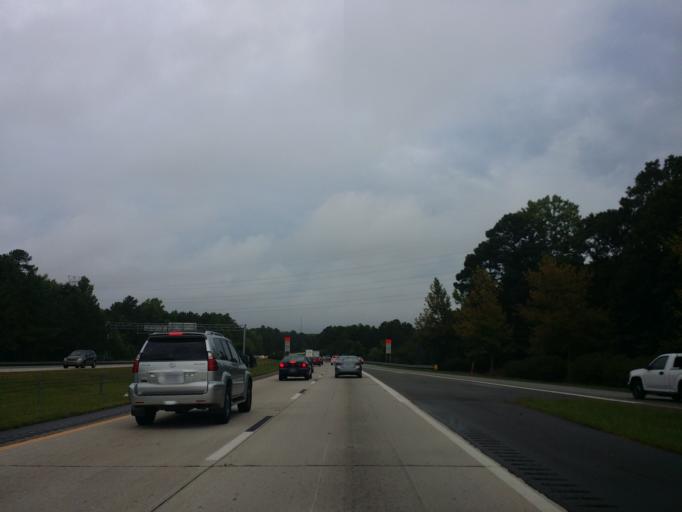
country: US
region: North Carolina
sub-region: Durham County
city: Durham
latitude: 35.9418
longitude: -78.8602
